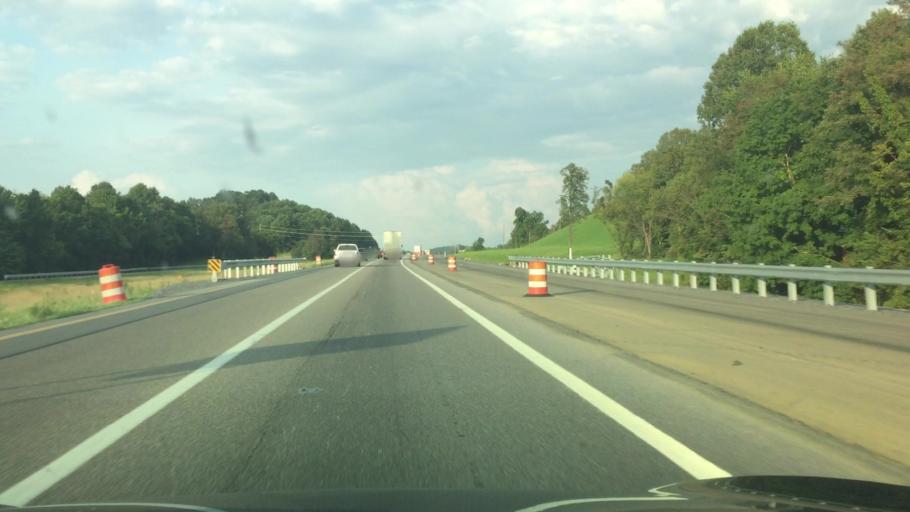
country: US
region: Tennessee
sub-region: Sullivan County
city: Colonial Heights
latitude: 36.5034
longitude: -82.4435
